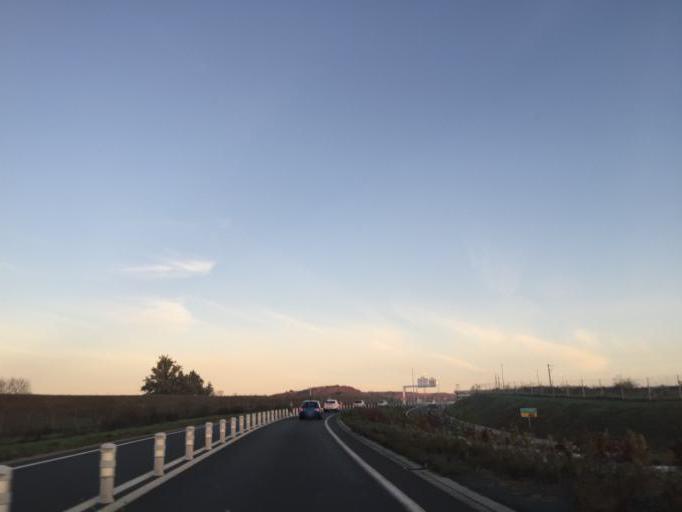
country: FR
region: Rhone-Alpes
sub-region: Departement de la Loire
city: Balbigny
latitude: 45.8374
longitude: 4.1655
